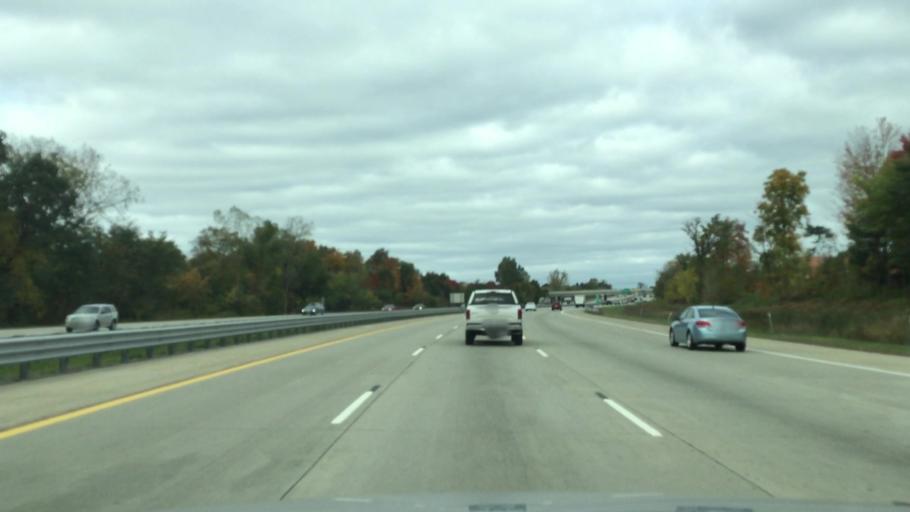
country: US
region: Michigan
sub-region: Oakland County
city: Rochester Hills
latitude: 42.6322
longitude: -83.1415
